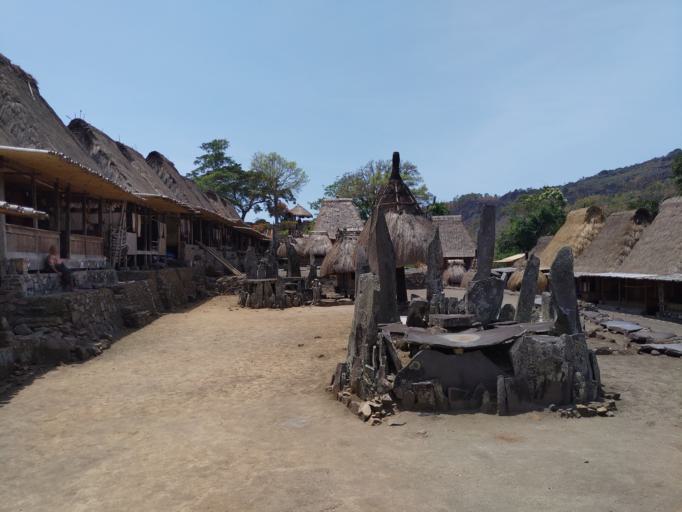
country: ID
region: East Nusa Tenggara
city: Gurusina
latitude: -8.8776
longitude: 120.9859
